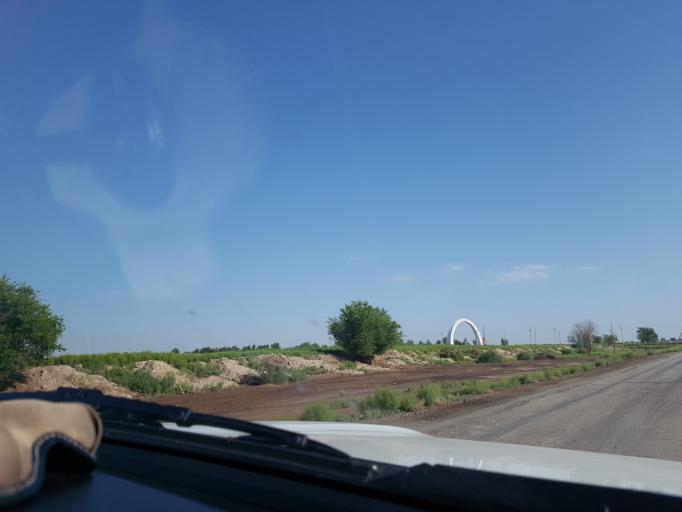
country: TM
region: Dasoguz
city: Koeneuergench
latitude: 41.8606
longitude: 58.7054
